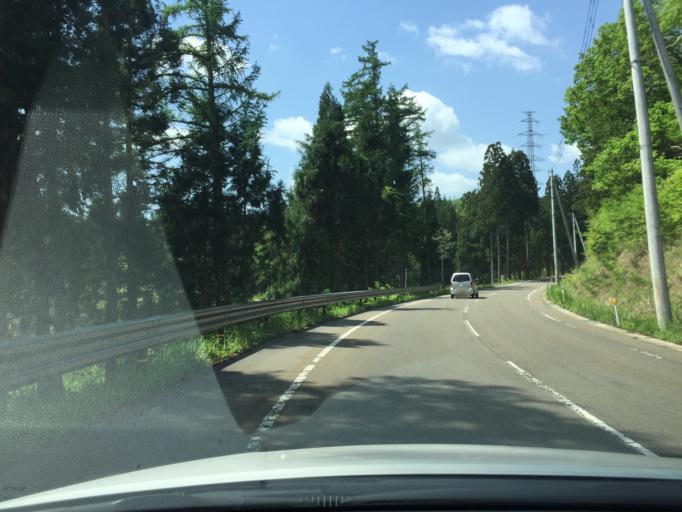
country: JP
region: Niigata
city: Tochio-honcho
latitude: 37.4700
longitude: 139.0357
